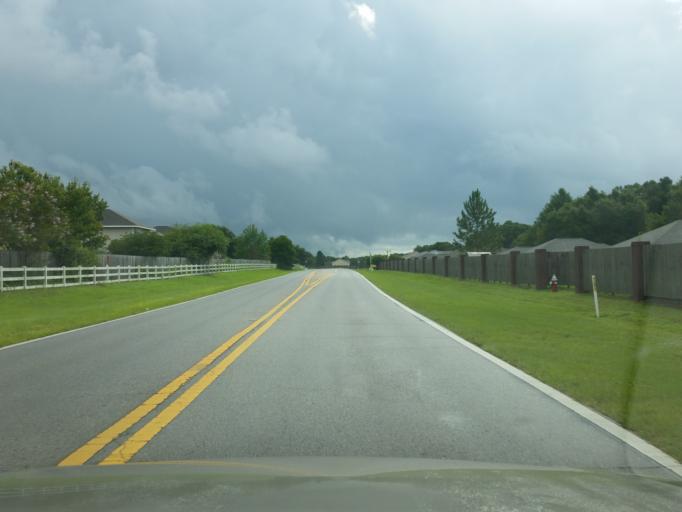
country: US
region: Florida
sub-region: Escambia County
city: West Pensacola
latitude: 30.4468
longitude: -87.2826
